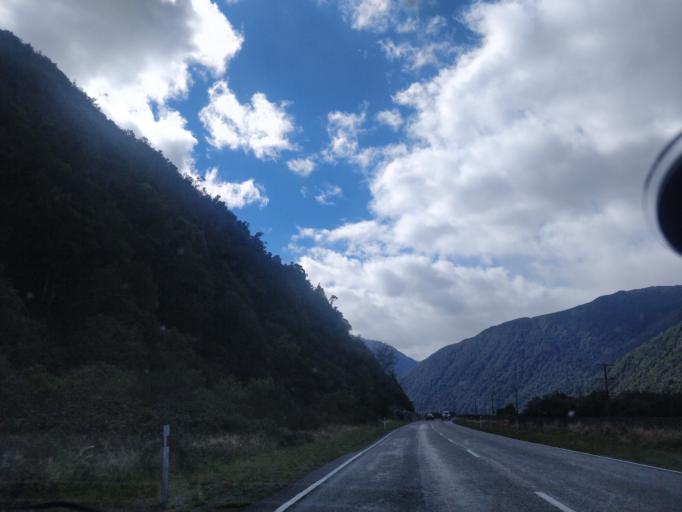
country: NZ
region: West Coast
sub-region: Grey District
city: Greymouth
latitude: -42.7909
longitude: 171.5967
